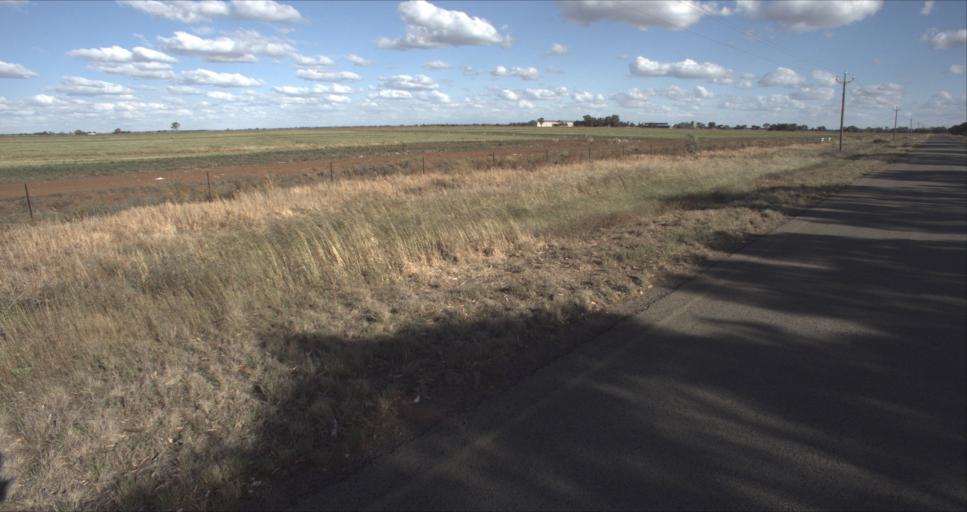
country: AU
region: New South Wales
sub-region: Leeton
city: Leeton
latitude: -34.5441
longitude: 146.2797
